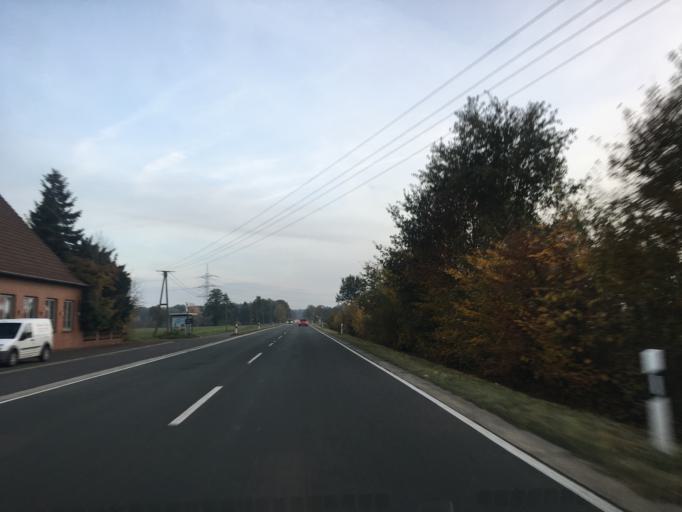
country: DE
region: North Rhine-Westphalia
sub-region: Regierungsbezirk Munster
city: Altenberge
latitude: 52.0850
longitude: 7.4249
